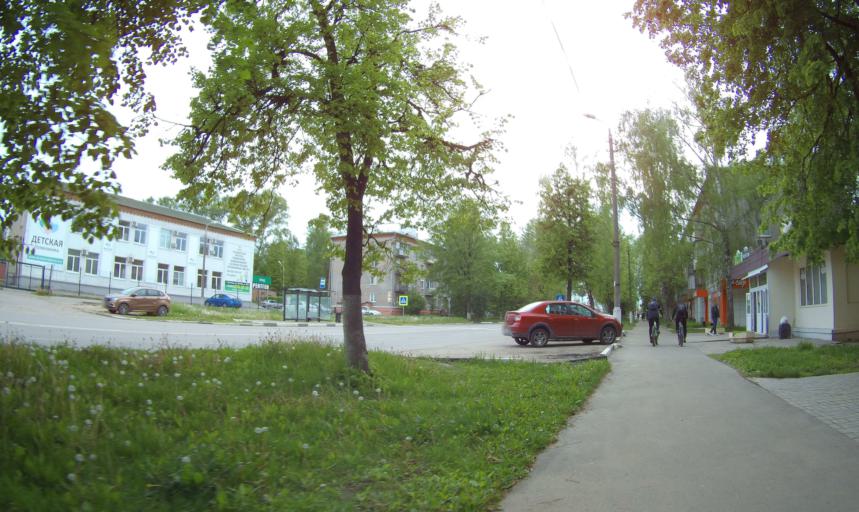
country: RU
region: Moskovskaya
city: Kolomna
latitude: 55.0880
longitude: 38.7642
